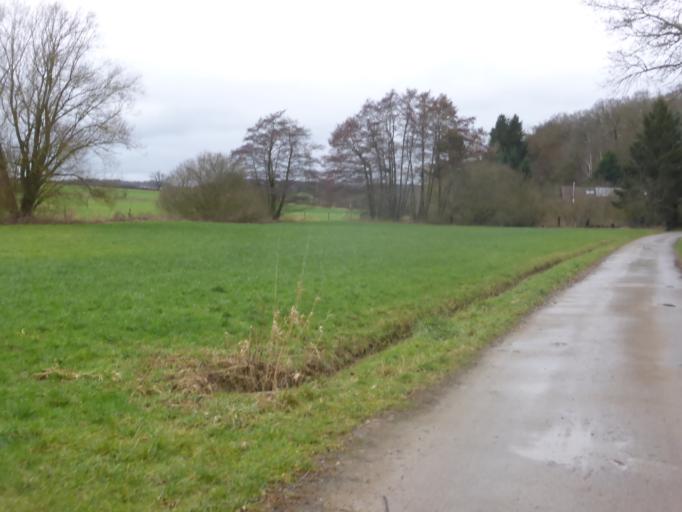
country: LU
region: Luxembourg
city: Bergem
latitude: 49.5366
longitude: 6.0514
